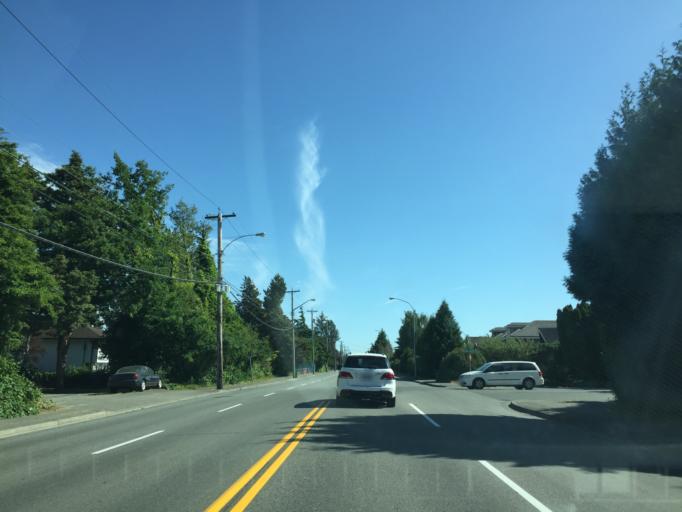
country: CA
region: British Columbia
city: Richmond
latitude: 49.1542
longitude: -123.1367
